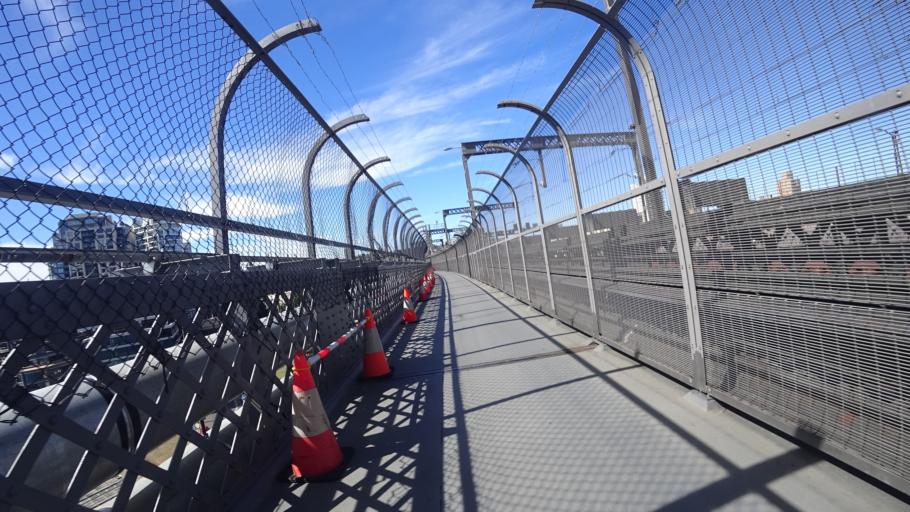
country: AU
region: New South Wales
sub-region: North Sydney
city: Milsons Point
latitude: -33.8499
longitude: 151.2119
